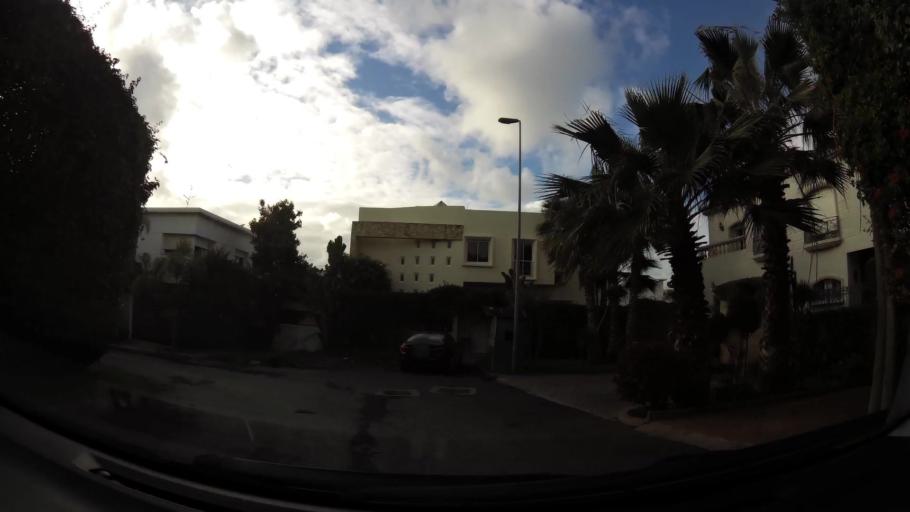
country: MA
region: Grand Casablanca
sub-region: Casablanca
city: Casablanca
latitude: 33.5724
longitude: -7.6933
